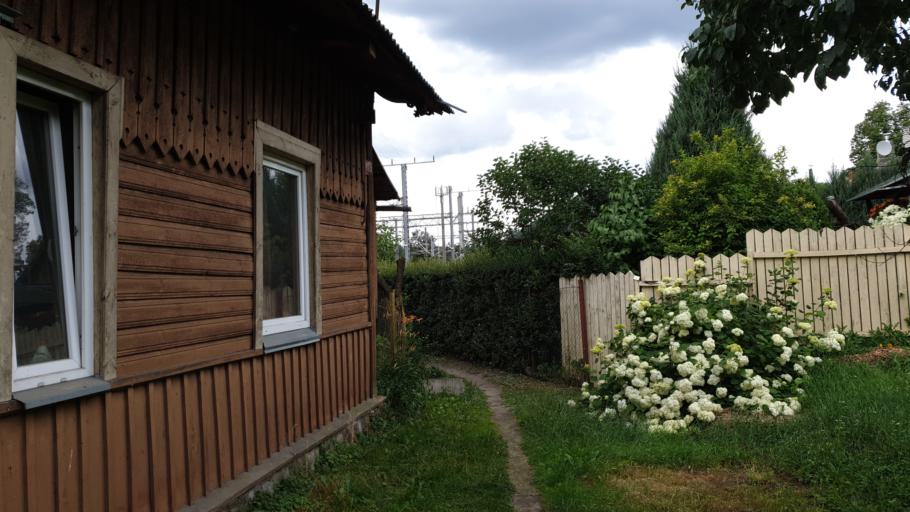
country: LT
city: Skaidiskes
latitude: 54.6940
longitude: 25.4036
